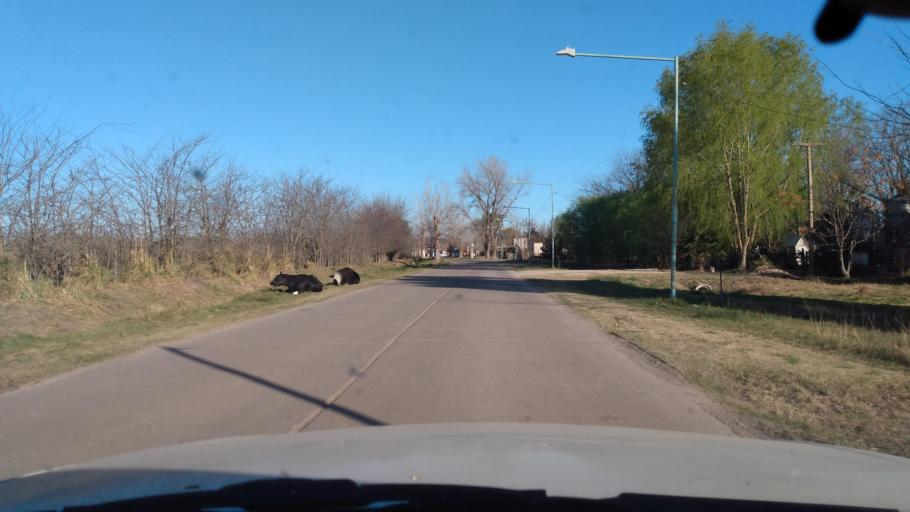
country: AR
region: Buenos Aires
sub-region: Partido de Lujan
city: Lujan
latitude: -34.6199
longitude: -59.2576
